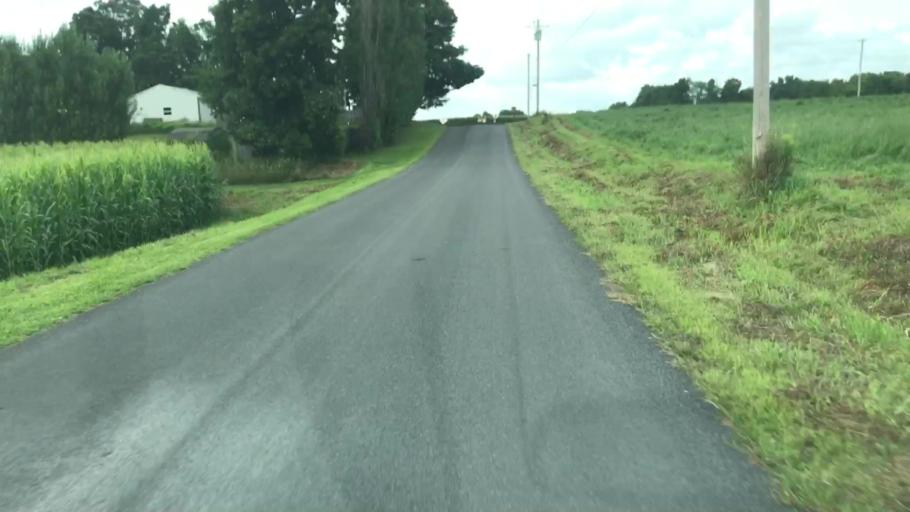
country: US
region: New York
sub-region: Cayuga County
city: Auburn
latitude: 42.9836
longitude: -76.5104
